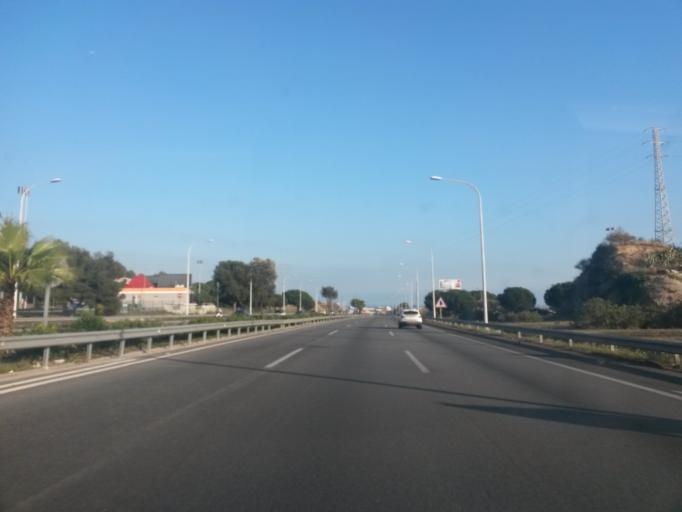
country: ES
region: Catalonia
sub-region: Provincia de Barcelona
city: Teia
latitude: 41.4925
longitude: 2.3325
